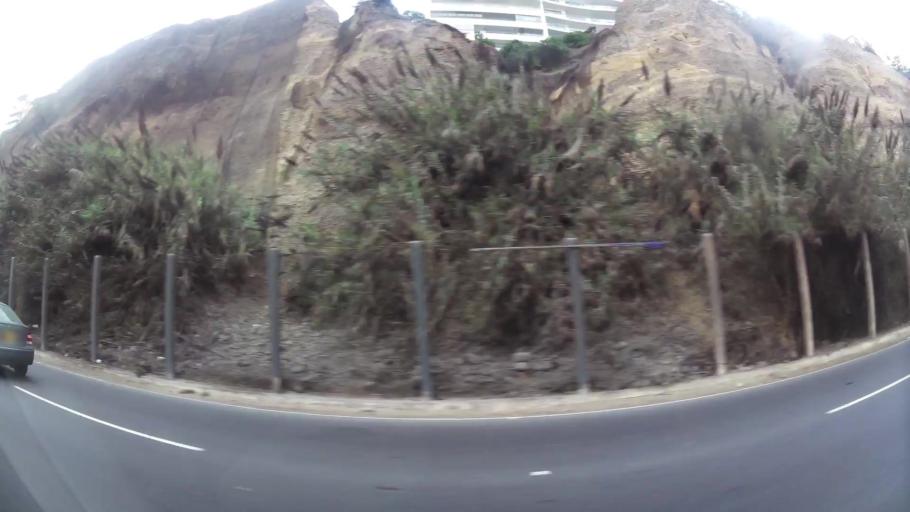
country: PE
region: Lima
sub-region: Lima
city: Surco
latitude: -12.1476
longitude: -77.0248
